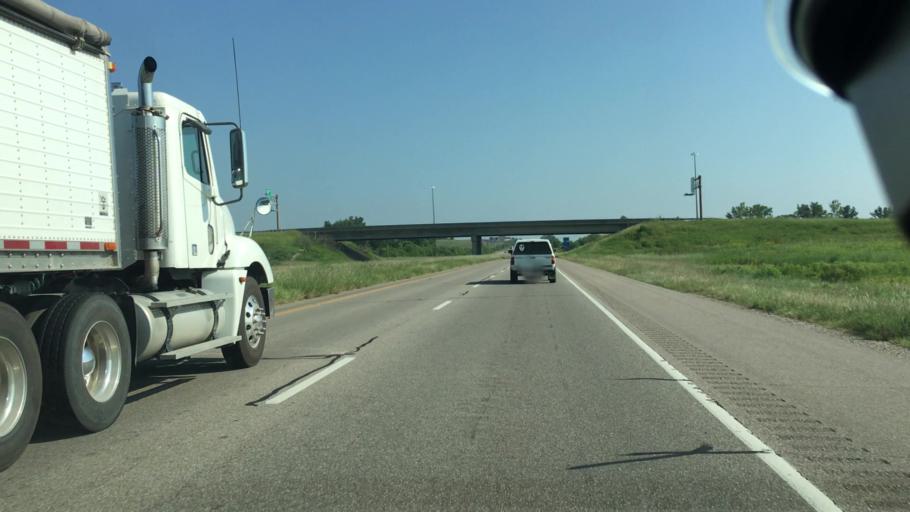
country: US
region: Indiana
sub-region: Gibson County
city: Fort Branch
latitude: 38.2726
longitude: -87.5676
